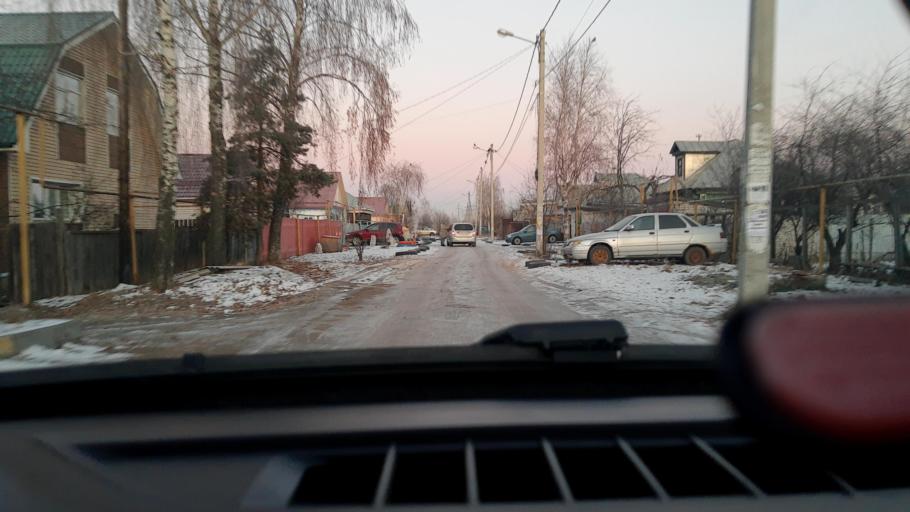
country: RU
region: Nizjnij Novgorod
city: Nizhniy Novgorod
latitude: 56.2784
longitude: 43.8846
